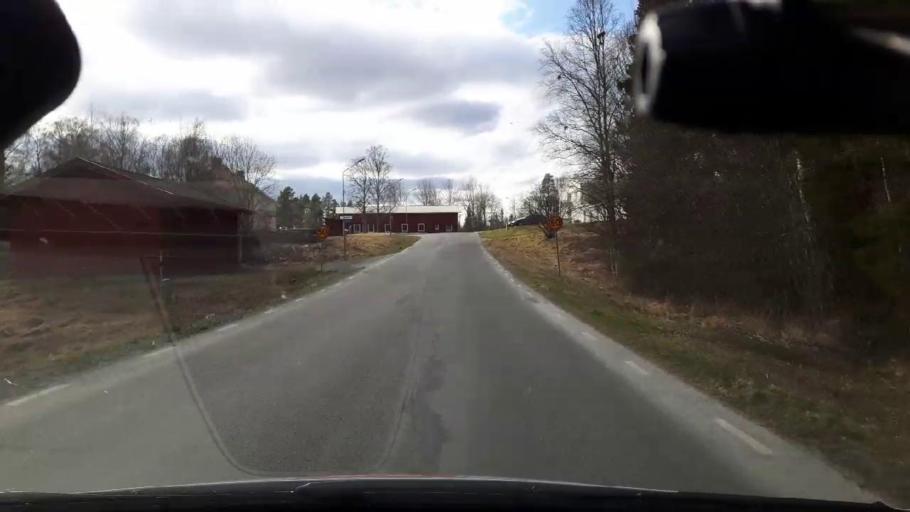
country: SE
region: Jaemtland
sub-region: OEstersunds Kommun
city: Ostersund
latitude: 62.9940
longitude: 14.5794
